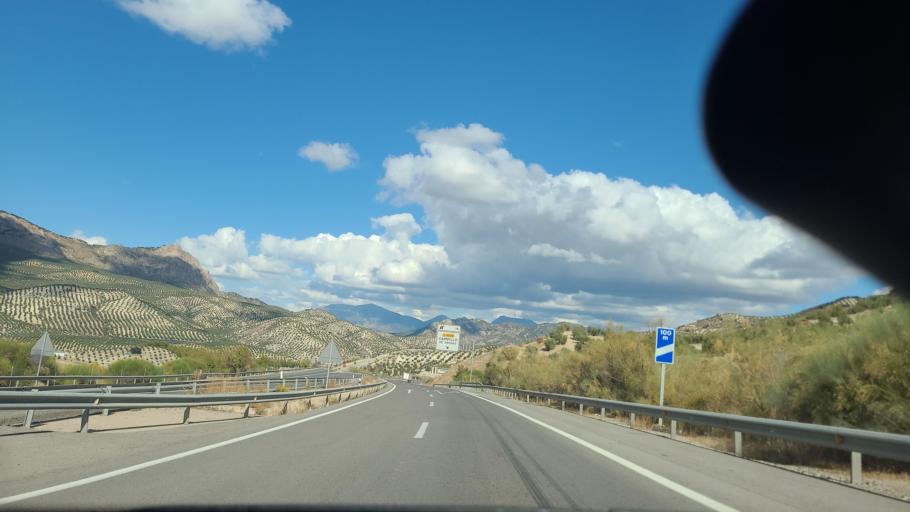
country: ES
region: Andalusia
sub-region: Provincia de Jaen
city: Campillo de Arenas
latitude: 37.5517
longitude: -3.6300
